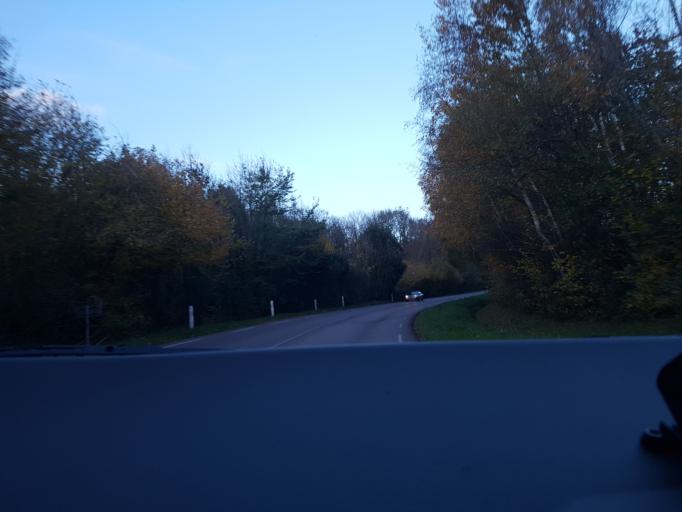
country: FR
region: Lower Normandy
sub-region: Departement du Calvados
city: Ablon
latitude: 49.3154
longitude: 0.2620
